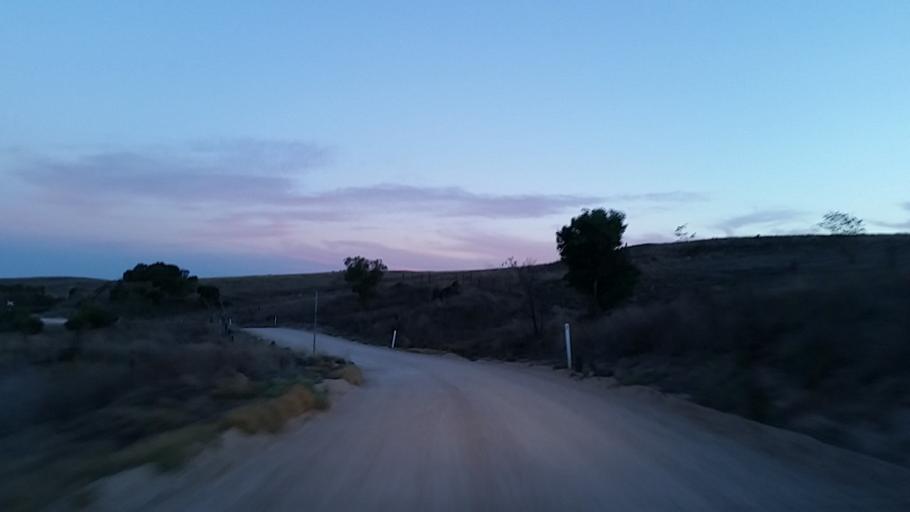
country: AU
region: South Australia
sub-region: Mount Barker
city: Callington
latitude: -35.0995
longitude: 138.9977
